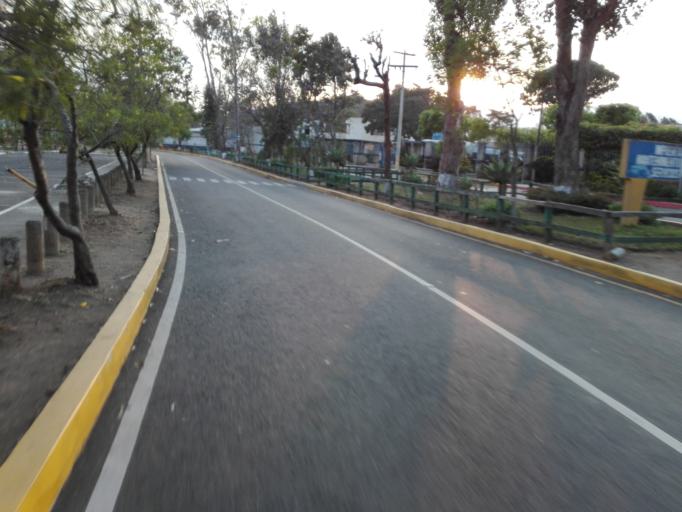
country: GT
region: Guatemala
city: Santa Catarina Pinula
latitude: 14.5850
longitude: -90.5556
